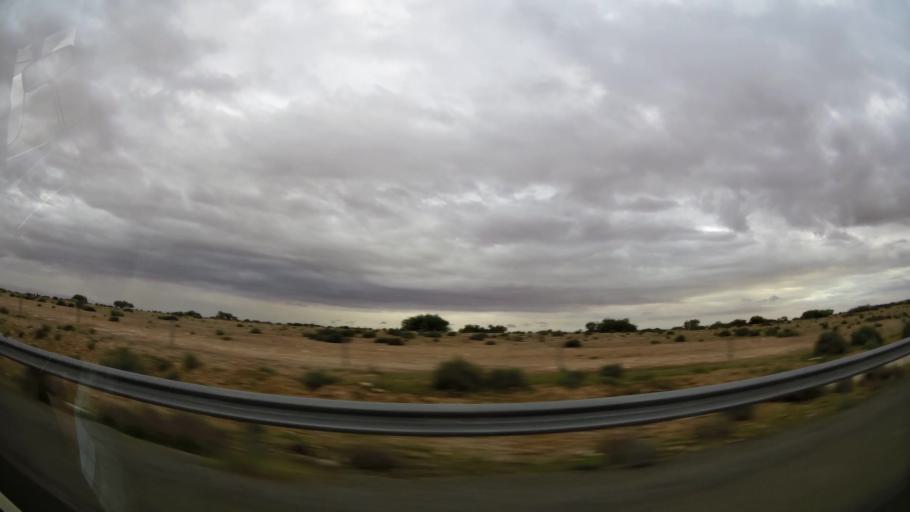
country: MA
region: Taza-Al Hoceima-Taounate
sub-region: Taza
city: Guercif
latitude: 34.3052
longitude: -3.6397
